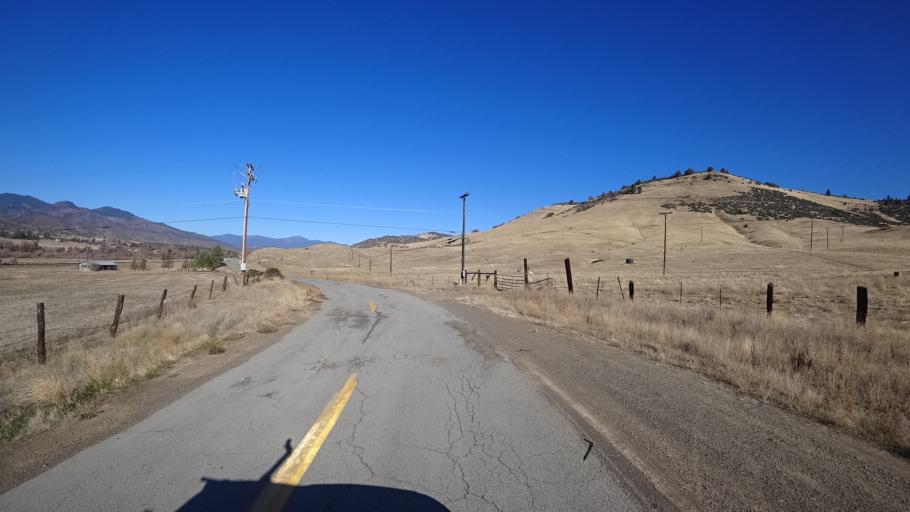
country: US
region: California
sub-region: Siskiyou County
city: Montague
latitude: 41.9010
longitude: -122.5445
